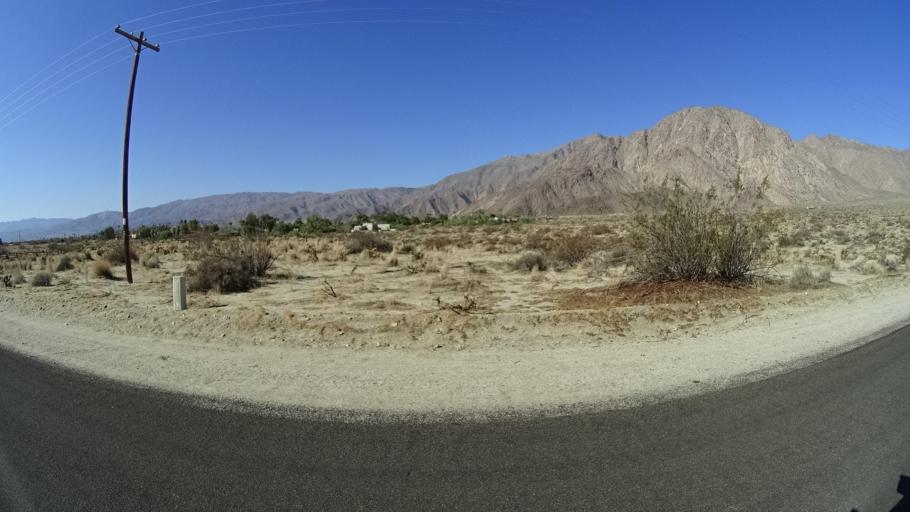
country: US
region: California
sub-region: San Diego County
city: Borrego Springs
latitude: 33.2992
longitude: -116.3853
